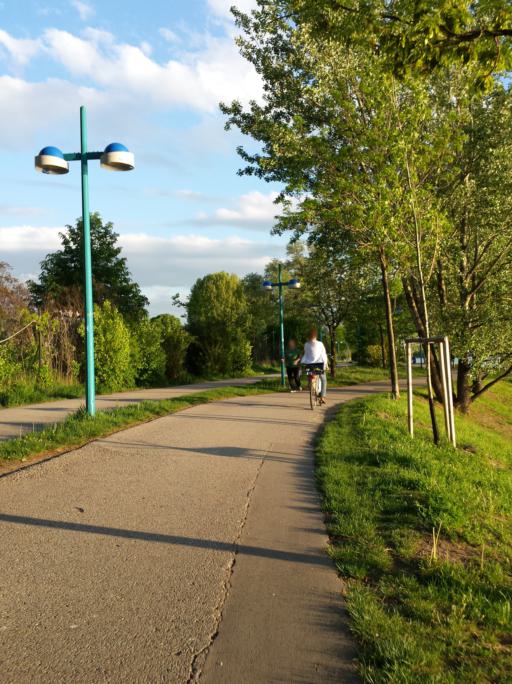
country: AT
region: Vienna
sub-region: Wien Stadt
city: Vienna
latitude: 48.2263
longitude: 16.4364
